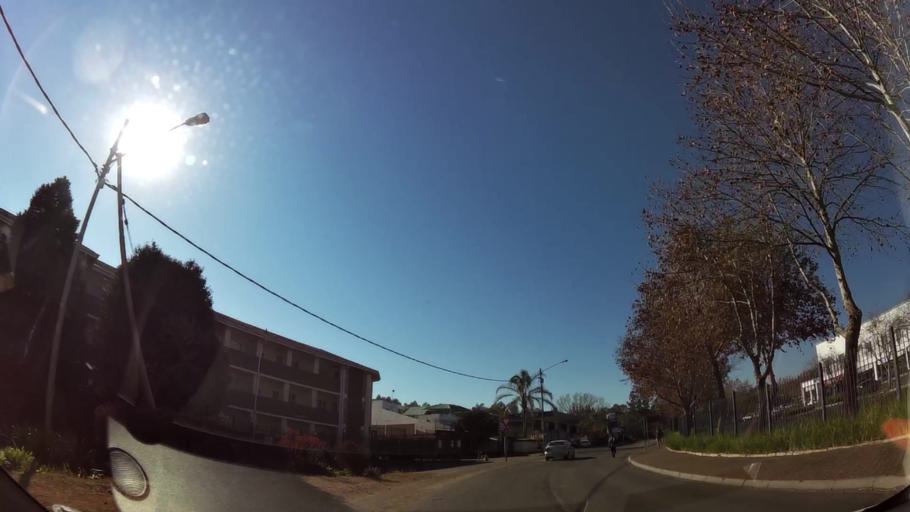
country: ZA
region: Gauteng
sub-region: City of Tshwane Metropolitan Municipality
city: Centurion
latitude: -25.8551
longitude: 28.2164
